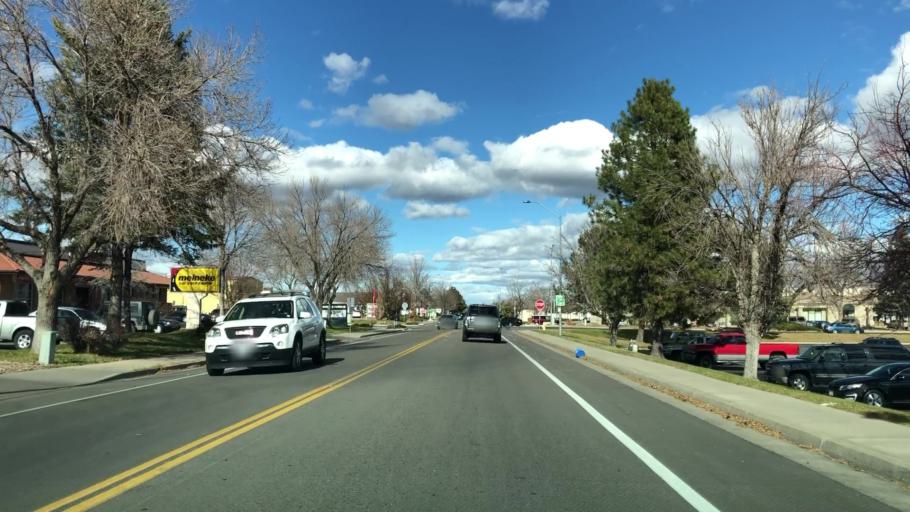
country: US
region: Colorado
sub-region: Larimer County
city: Fort Collins
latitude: 40.5277
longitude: -105.0795
